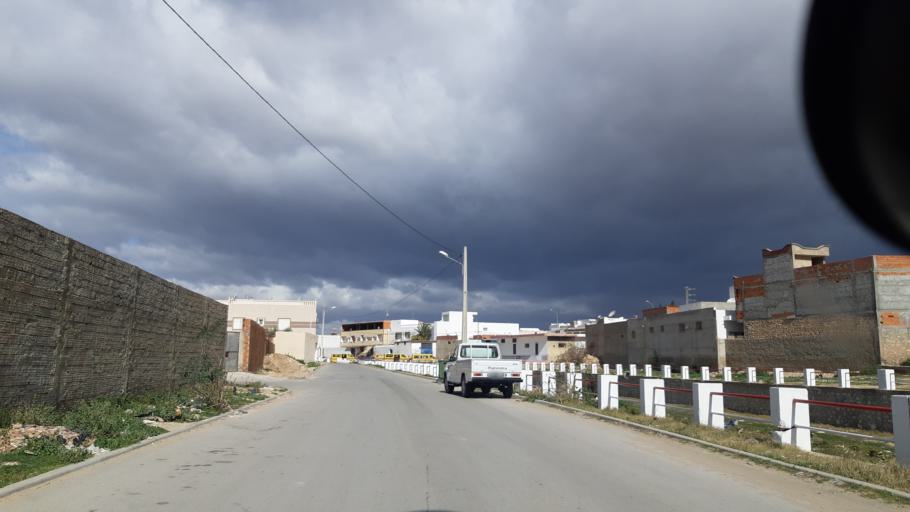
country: TN
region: Susah
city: Akouda
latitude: 35.8748
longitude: 10.5417
